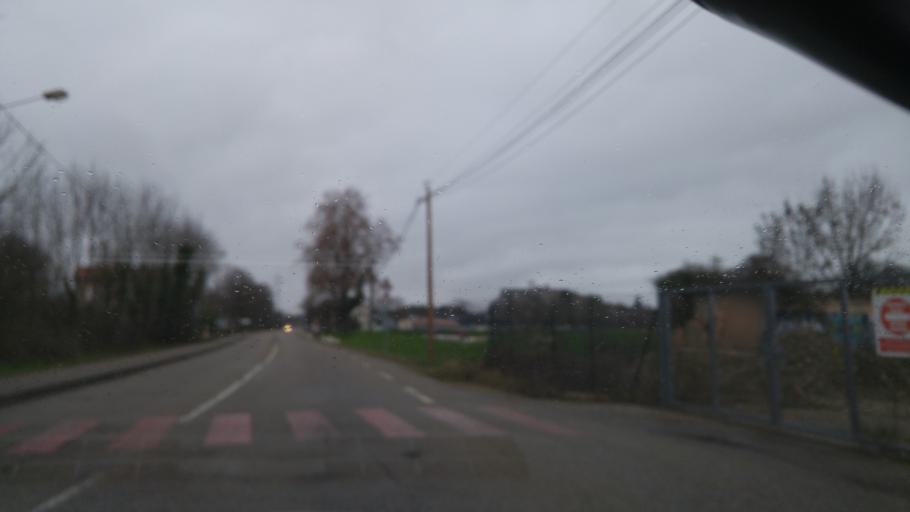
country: FR
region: Rhone-Alpes
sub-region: Departement de l'Isere
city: Villefontaine
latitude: 45.6239
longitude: 5.1545
